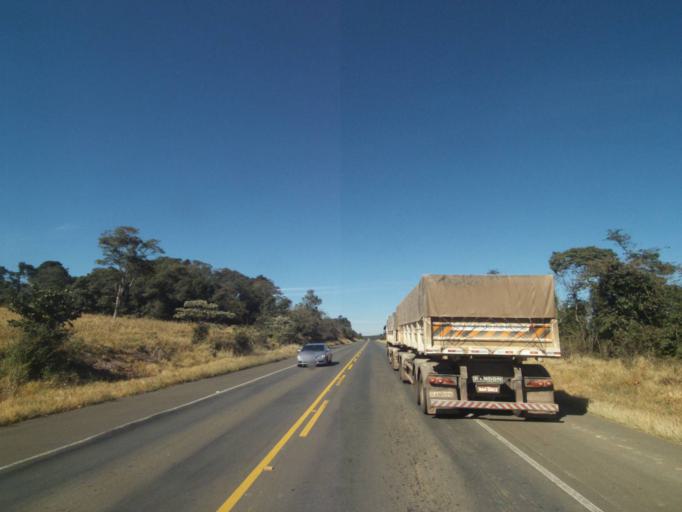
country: BR
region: Parana
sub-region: Tibagi
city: Tibagi
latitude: -24.7640
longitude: -50.4697
